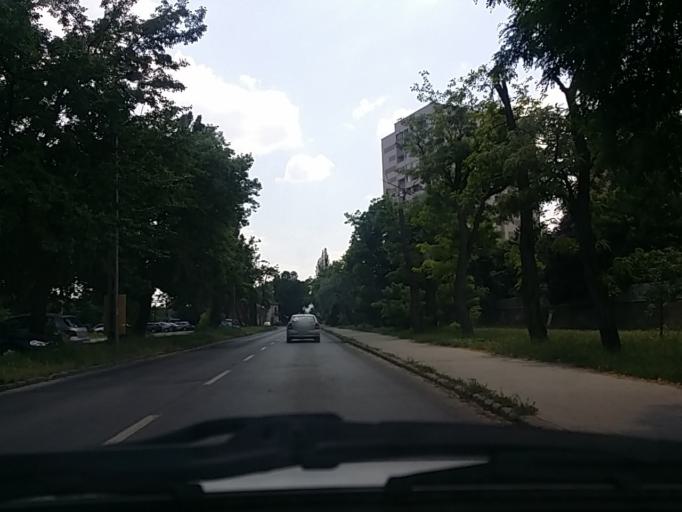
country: HU
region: Pest
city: Budakalasz
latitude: 47.5971
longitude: 19.0534
